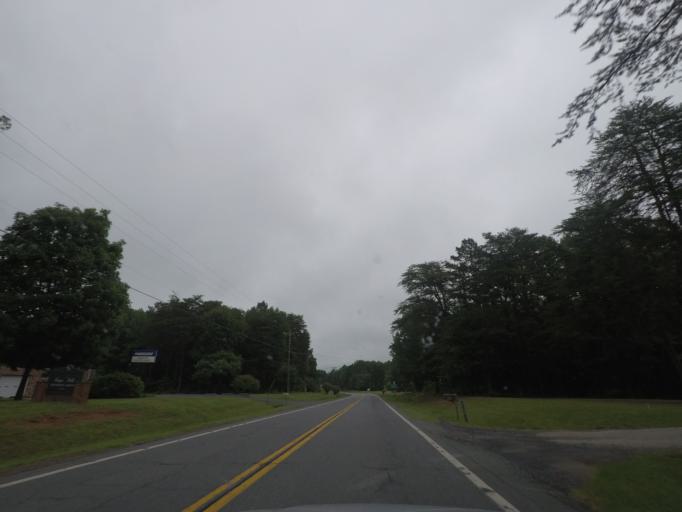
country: US
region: Virginia
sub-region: Fluvanna County
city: Weber City
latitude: 37.6545
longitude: -78.3523
